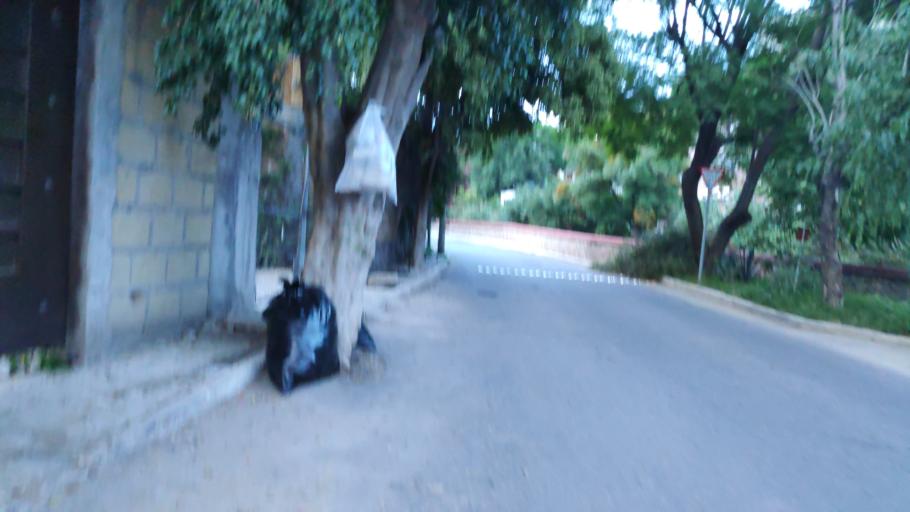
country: MX
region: Queretaro
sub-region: Queretaro
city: Santiago de Queretaro
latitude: 20.6023
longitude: -100.3645
